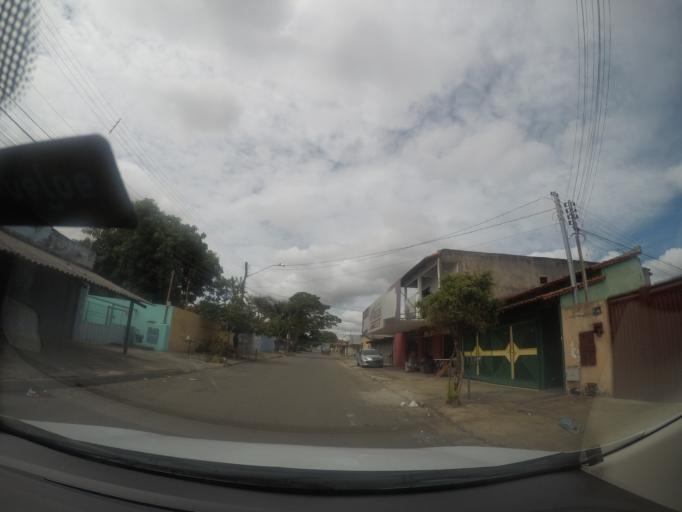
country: BR
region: Goias
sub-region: Goiania
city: Goiania
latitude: -16.6594
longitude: -49.3047
